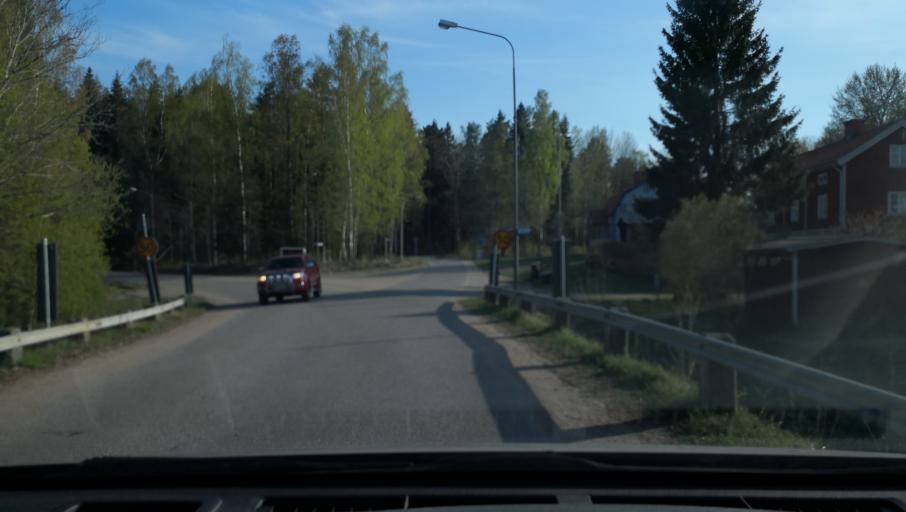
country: SE
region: Uppsala
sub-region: Heby Kommun
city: Tarnsjo
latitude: 60.2838
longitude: 16.8831
